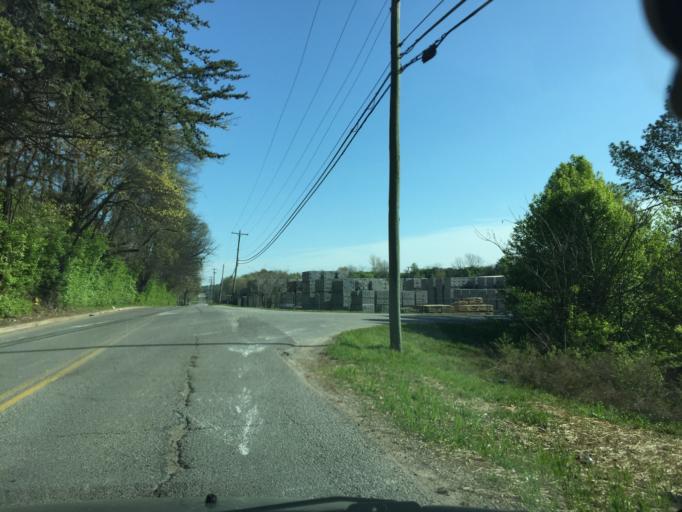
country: US
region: Tennessee
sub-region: Hamilton County
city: East Chattanooga
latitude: 35.0582
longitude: -85.2083
